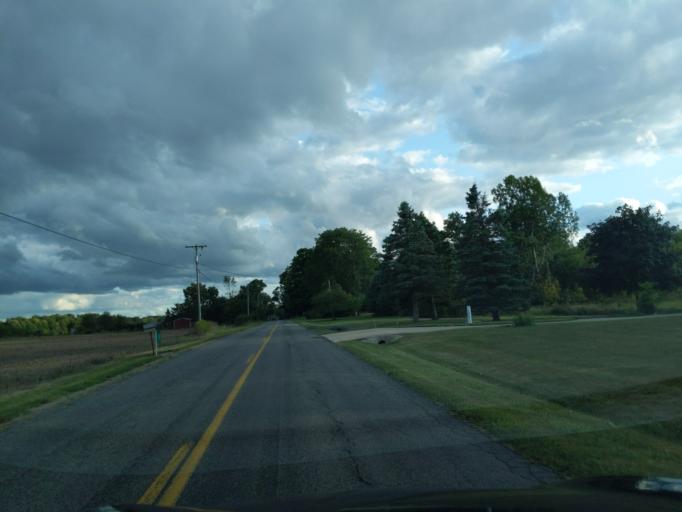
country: US
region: Michigan
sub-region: Eaton County
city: Dimondale
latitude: 42.5869
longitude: -84.5922
